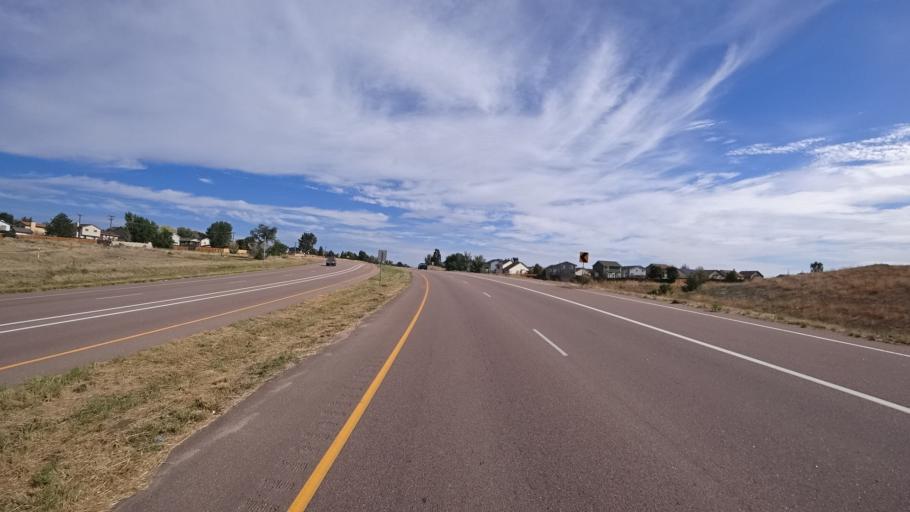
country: US
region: Colorado
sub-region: El Paso County
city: Security-Widefield
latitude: 38.7225
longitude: -104.6820
